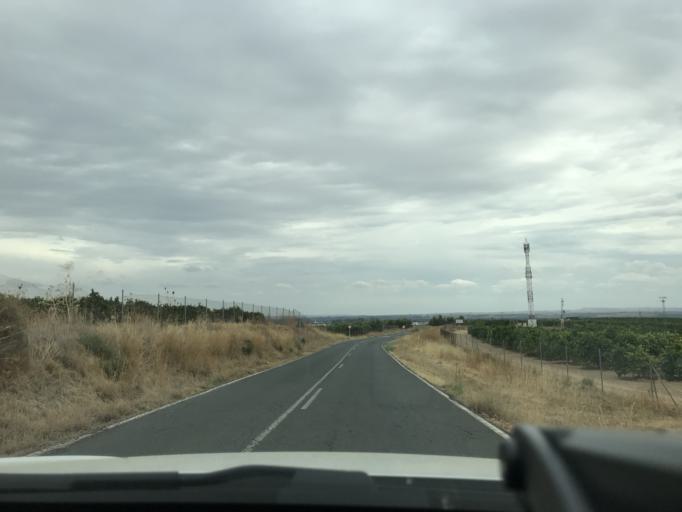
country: ES
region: Andalusia
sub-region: Provincia de Sevilla
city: Villanueva del Rio y Minas
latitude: 37.6411
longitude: -5.7047
